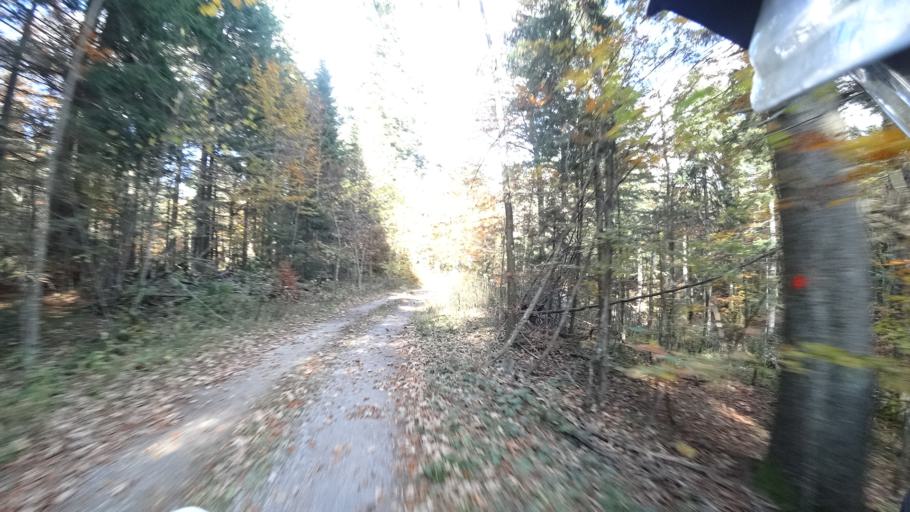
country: HR
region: Karlovacka
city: Plaski
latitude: 45.0404
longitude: 15.3402
